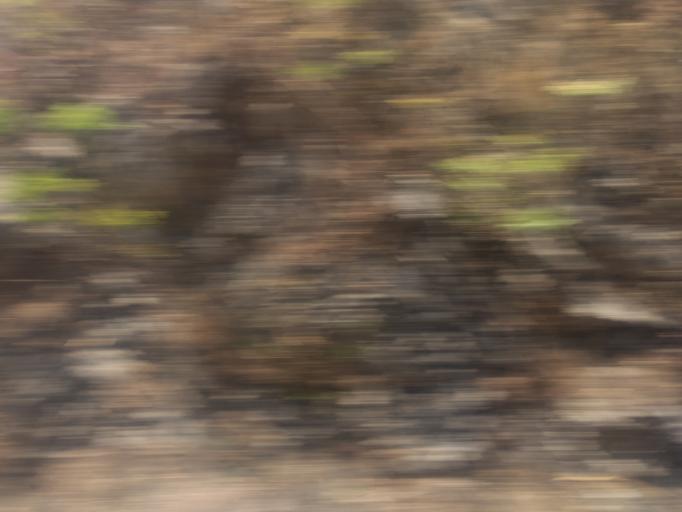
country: MX
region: Jalisco
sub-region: Tuxpan
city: La Higuera
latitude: 19.5007
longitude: -103.4425
